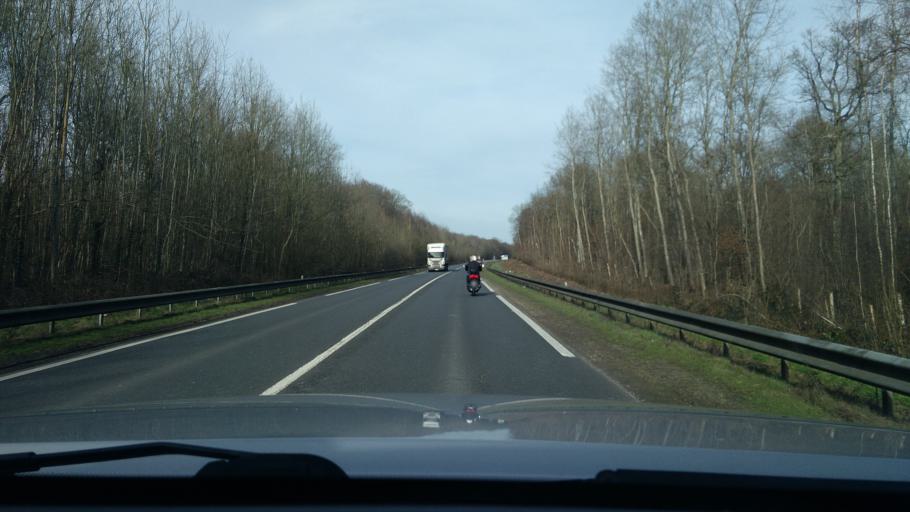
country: FR
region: Ile-de-France
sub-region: Departement de Seine-et-Marne
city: Chaumes-en-Brie
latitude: 48.6883
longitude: 2.8172
